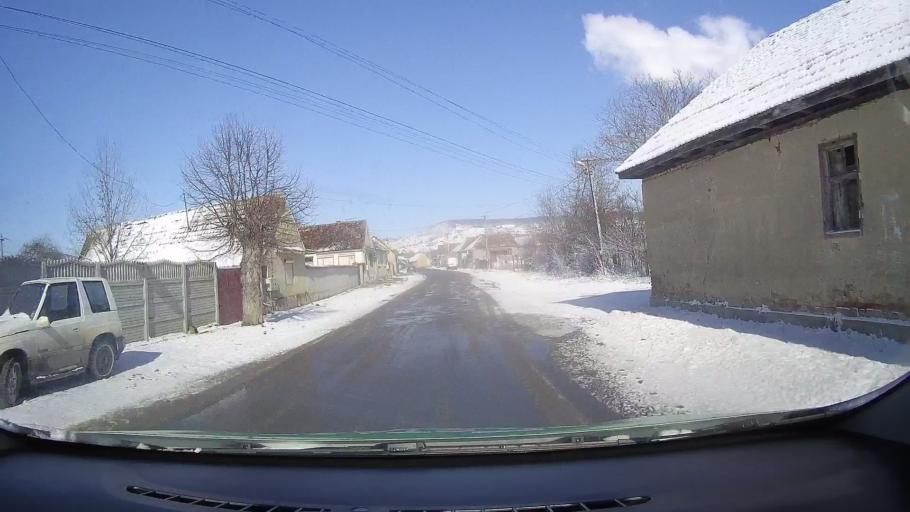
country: RO
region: Sibiu
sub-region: Comuna Avrig
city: Avrig
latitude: 45.7544
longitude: 24.3917
